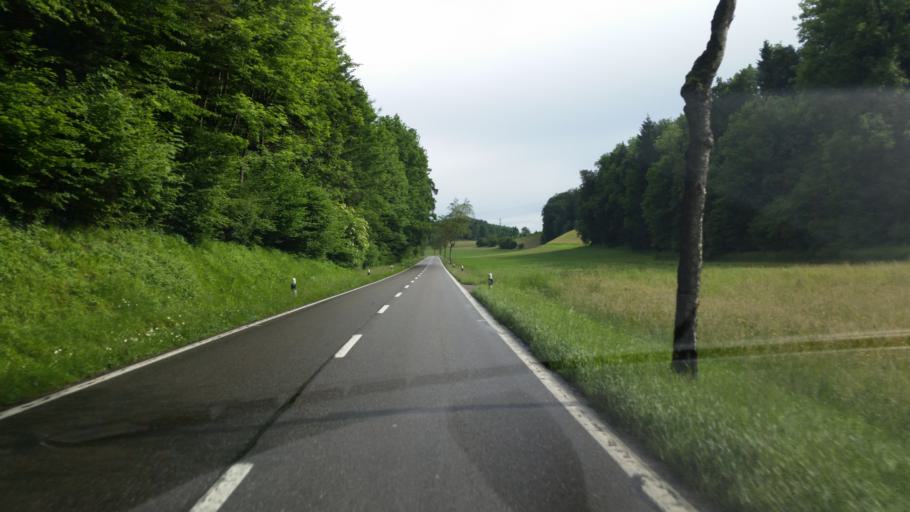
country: CH
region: Aargau
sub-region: Bezirk Bremgarten
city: Unterlunkhofen
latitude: 47.3164
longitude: 8.3542
